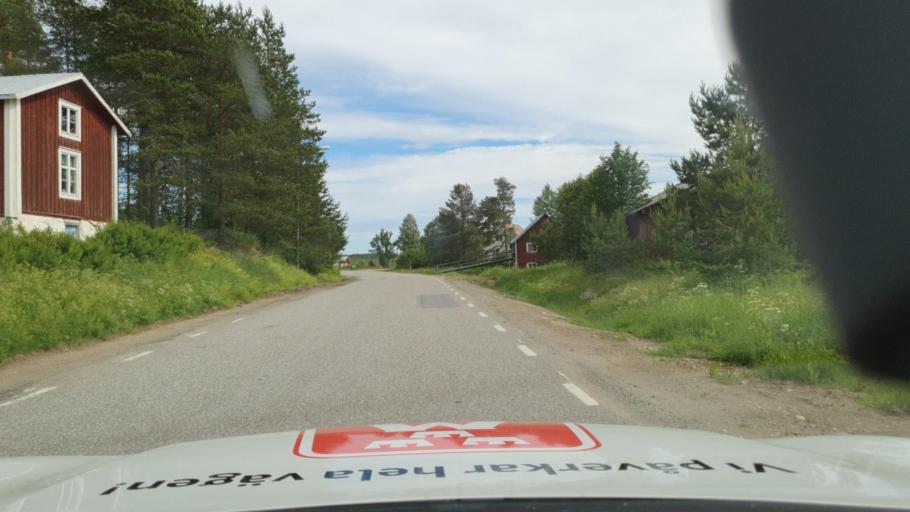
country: SE
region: Vaesterbotten
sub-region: Robertsfors Kommun
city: Robertsfors
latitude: 64.4018
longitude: 21.0158
